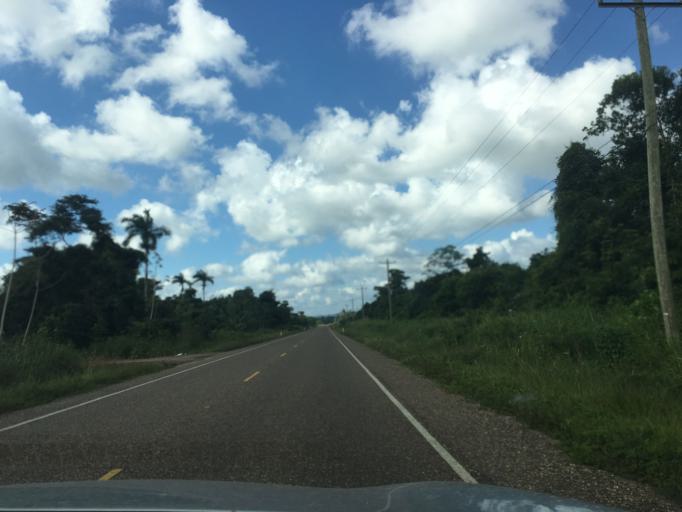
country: BZ
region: Stann Creek
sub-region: Dangriga
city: Dangriga
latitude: 16.8578
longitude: -88.3041
